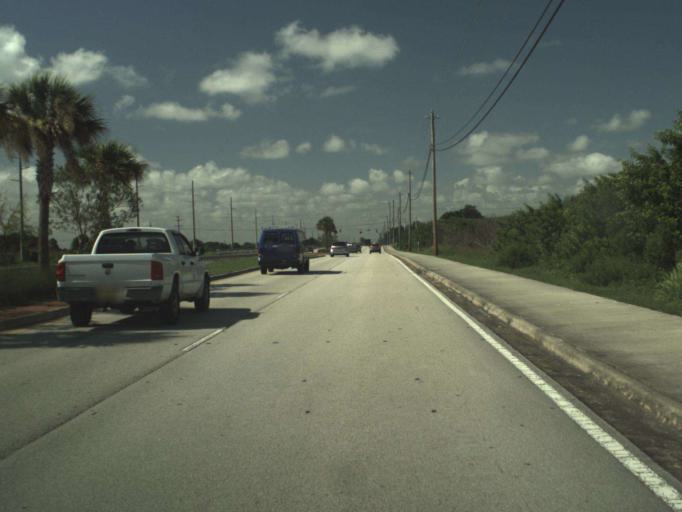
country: US
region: Florida
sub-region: Indian River County
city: Vero Beach South
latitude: 27.6200
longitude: -80.4472
